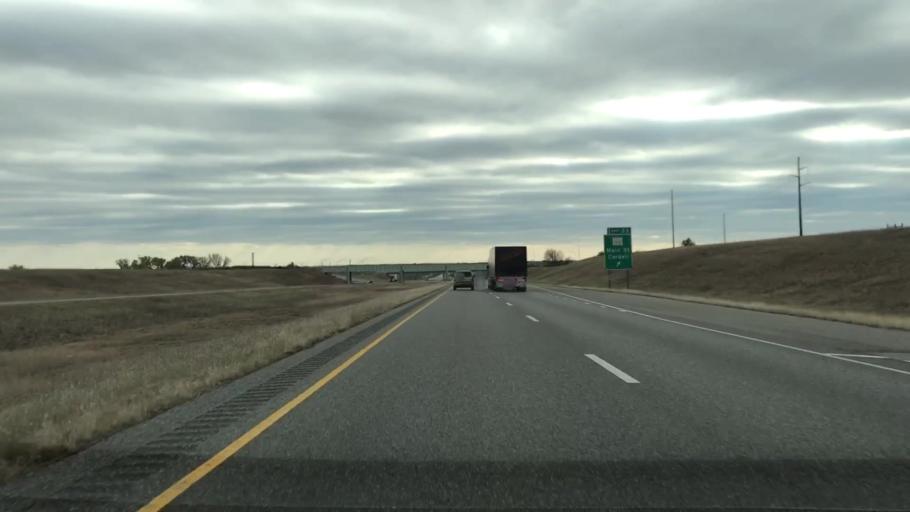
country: US
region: Oklahoma
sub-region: Beckham County
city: Sayre
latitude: 35.2975
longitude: -99.6186
